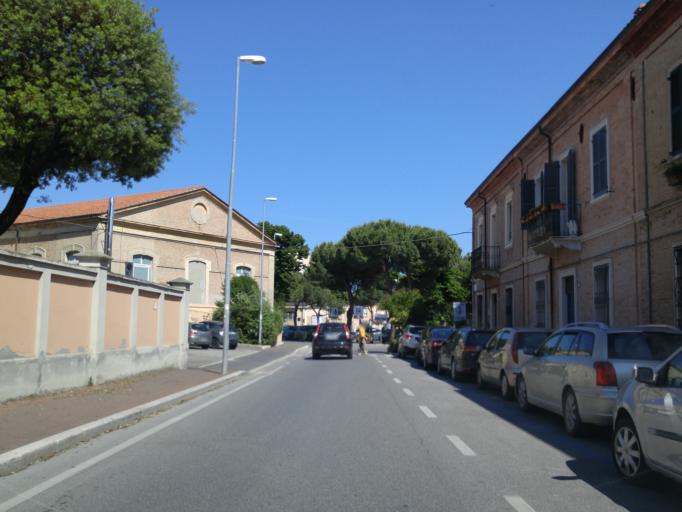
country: IT
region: The Marches
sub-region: Provincia di Pesaro e Urbino
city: Pesaro
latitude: 43.9064
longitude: 12.9112
